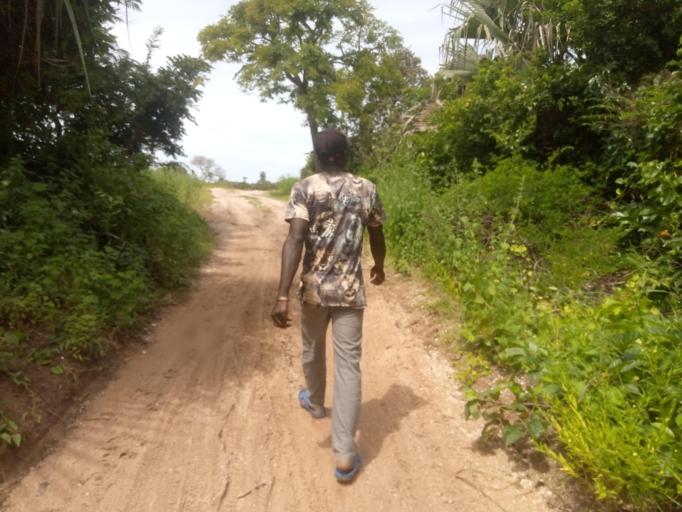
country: GM
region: Western
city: Gunjur
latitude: 13.0601
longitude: -16.7352
